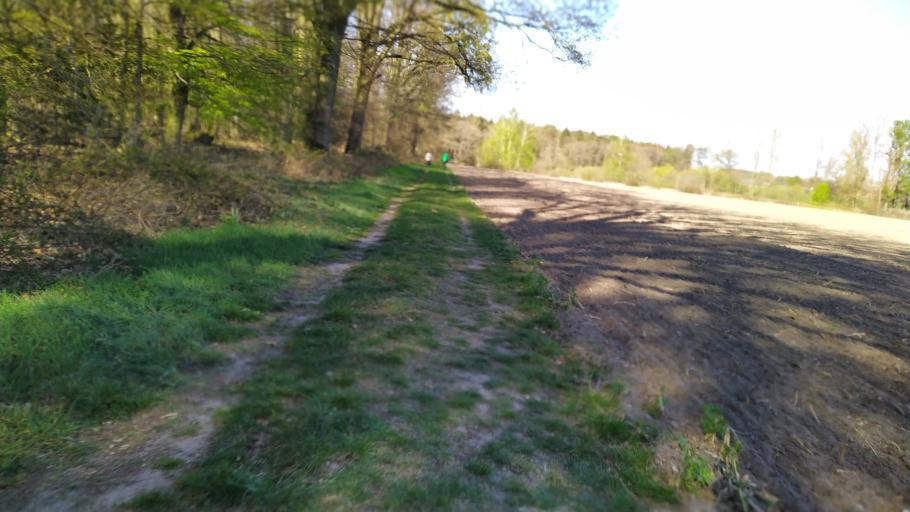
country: DE
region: Lower Saxony
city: Klein Meckelsen
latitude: 53.2983
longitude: 9.4320
